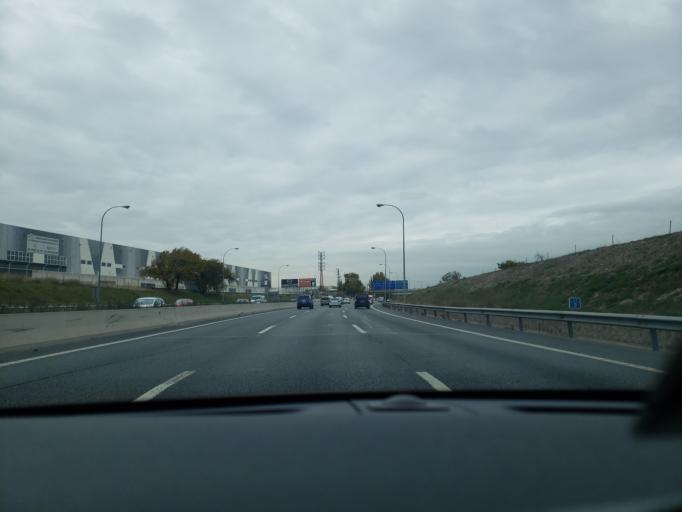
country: ES
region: Madrid
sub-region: Provincia de Madrid
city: Villaverde
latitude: 40.3637
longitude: -3.7016
